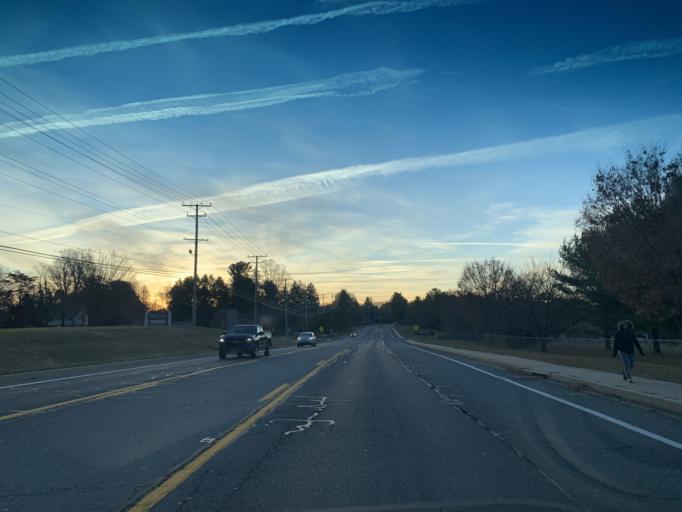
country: US
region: Maryland
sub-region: Harford County
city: Bel Air South
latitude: 39.5163
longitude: -76.3321
